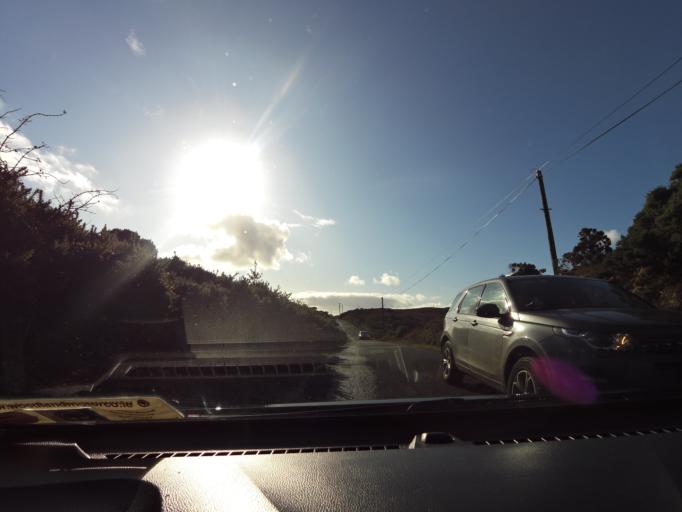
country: IE
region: Connaught
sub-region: Maigh Eo
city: Westport
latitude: 53.8969
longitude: -9.7960
